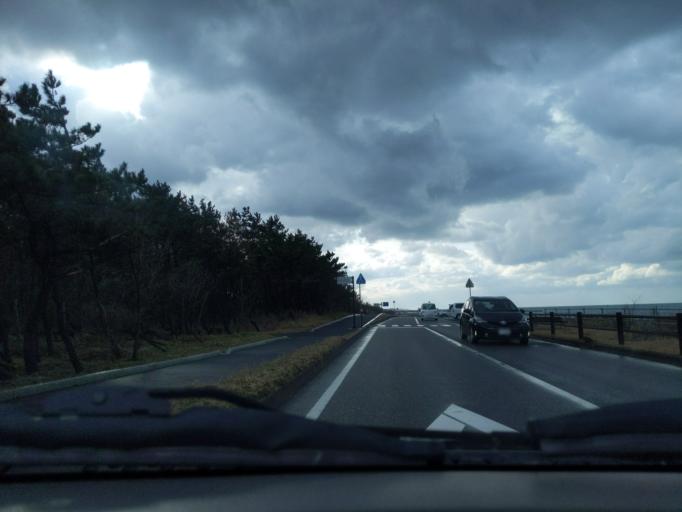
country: JP
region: Niigata
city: Niigata-shi
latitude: 37.9278
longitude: 139.0330
